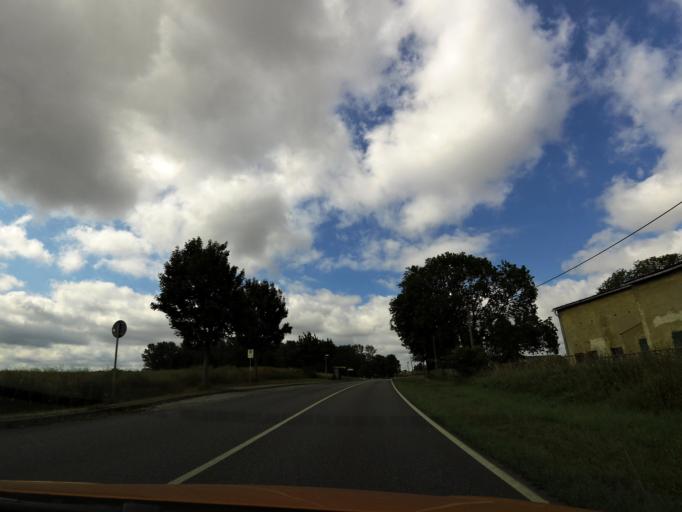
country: DE
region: Mecklenburg-Vorpommern
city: Krakow am See
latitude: 53.6965
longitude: 12.2751
